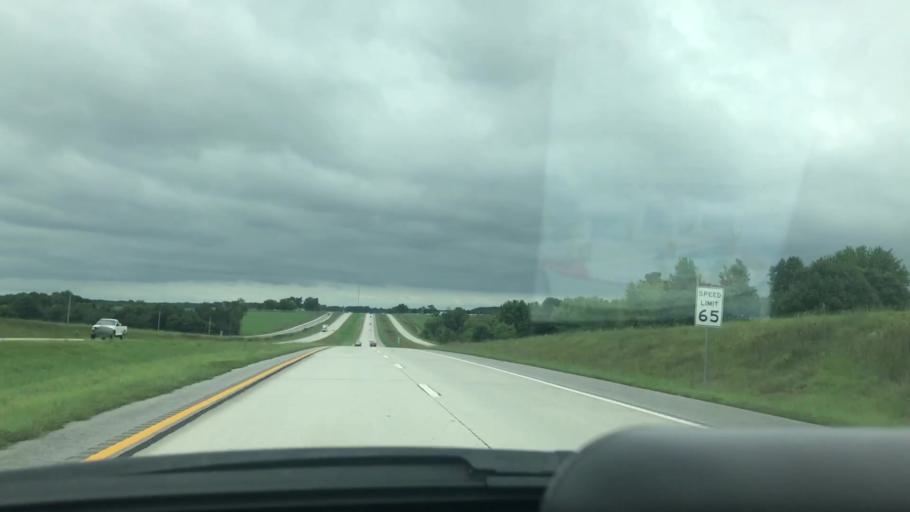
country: US
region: Missouri
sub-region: Greene County
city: Fair Grove
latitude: 37.4266
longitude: -93.1449
